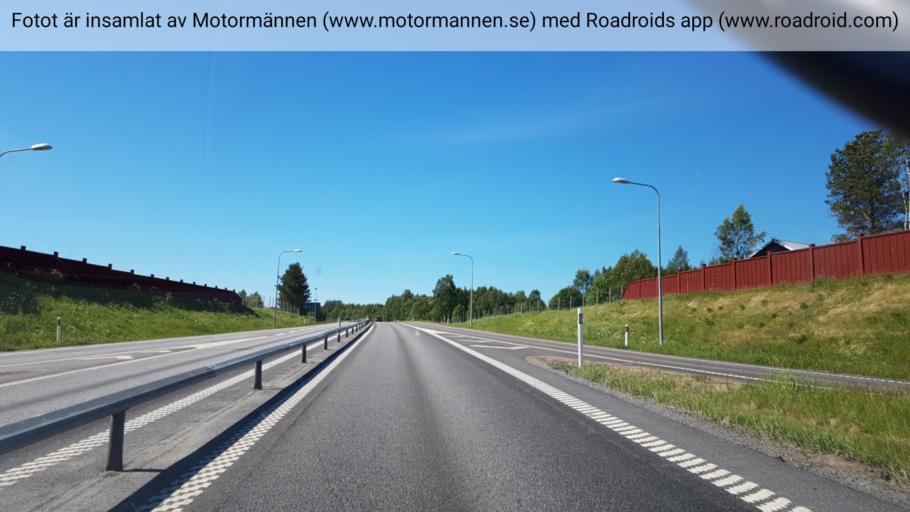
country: SE
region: Norrbotten
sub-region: Pitea Kommun
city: Rosvik
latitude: 65.5307
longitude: 21.7901
